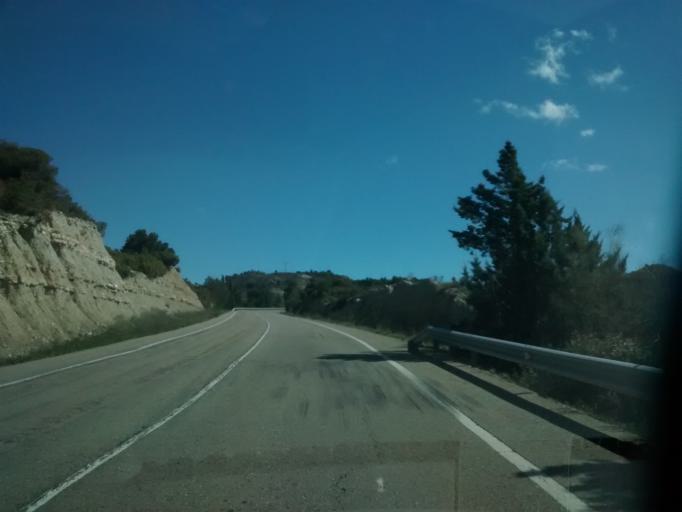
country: ES
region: Aragon
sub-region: Provincia de Huesca
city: Alcubierre
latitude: 41.8217
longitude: -0.5251
